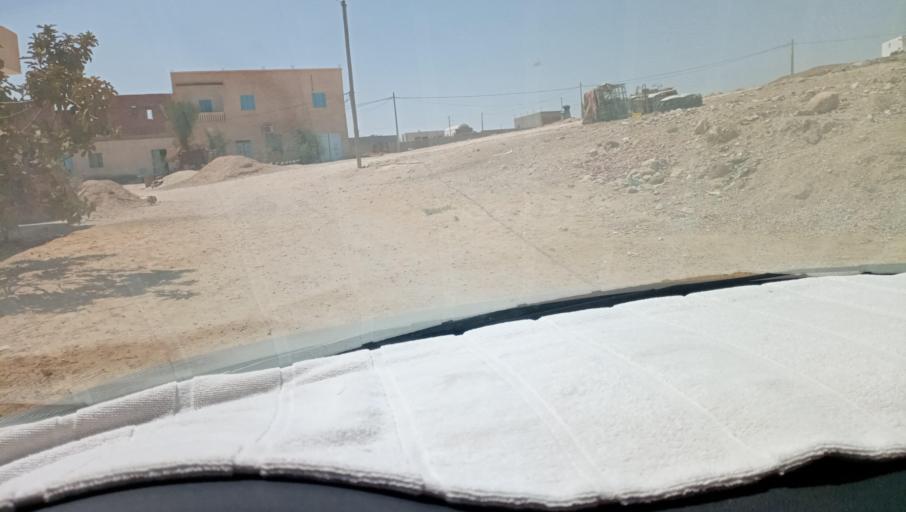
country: TN
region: Tataouine
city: Tataouine
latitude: 32.8454
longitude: 10.4733
